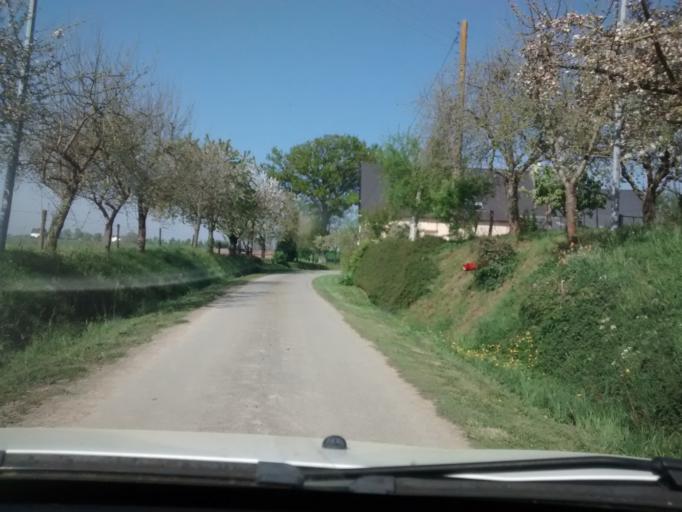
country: FR
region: Brittany
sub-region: Departement d'Ille-et-Vilaine
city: Javene
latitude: 48.3113
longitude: -1.2024
